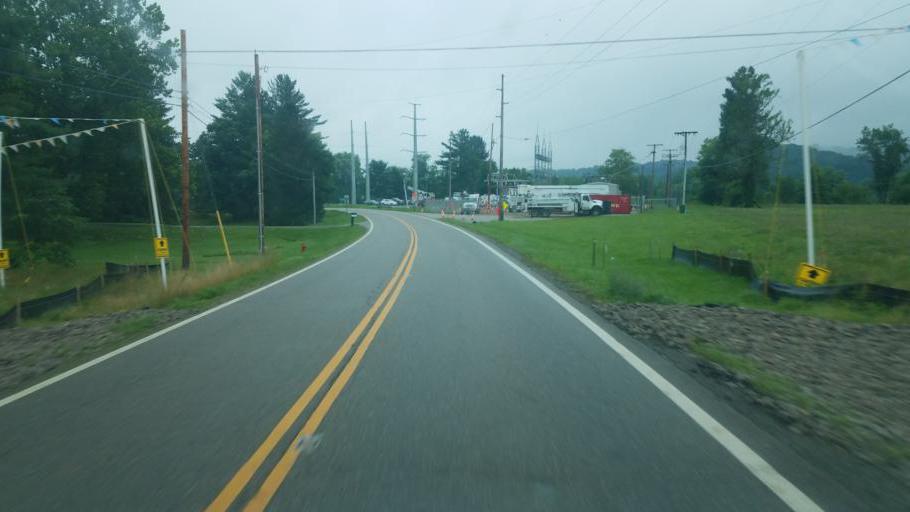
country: US
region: Ohio
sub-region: Tuscarawas County
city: Rockford
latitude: 40.4459
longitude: -81.2041
